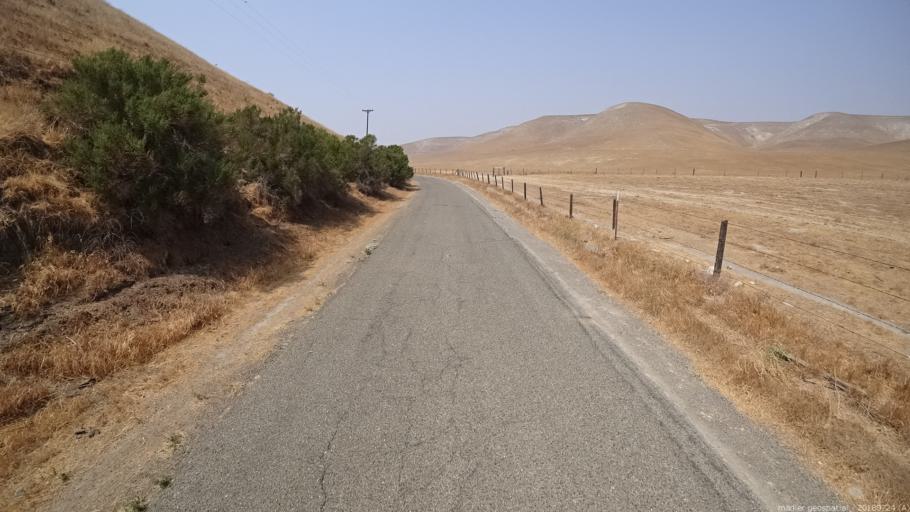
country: US
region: California
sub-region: Monterey County
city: King City
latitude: 36.1989
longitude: -121.0059
